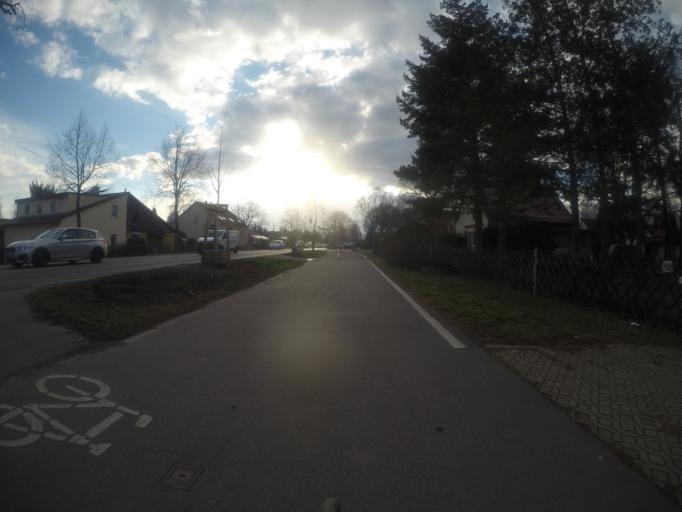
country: DE
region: Berlin
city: Falkenberg
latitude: 52.5706
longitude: 13.5570
